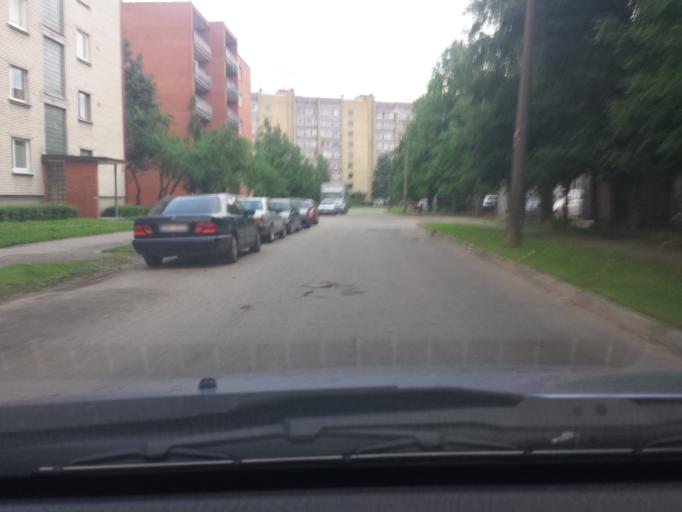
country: LV
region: Riga
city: Jaunciems
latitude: 56.9668
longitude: 24.1861
